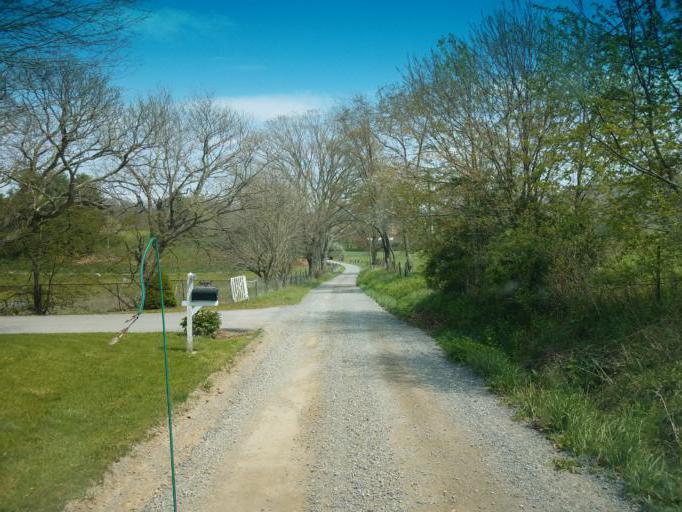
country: US
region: Virginia
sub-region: Smyth County
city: Marion
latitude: 36.7789
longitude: -81.4576
